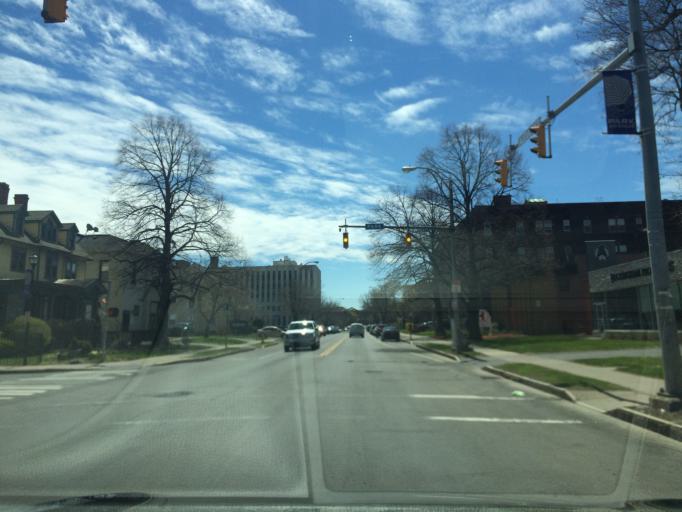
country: US
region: New York
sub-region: Monroe County
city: Rochester
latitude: 43.1526
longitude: -77.5957
